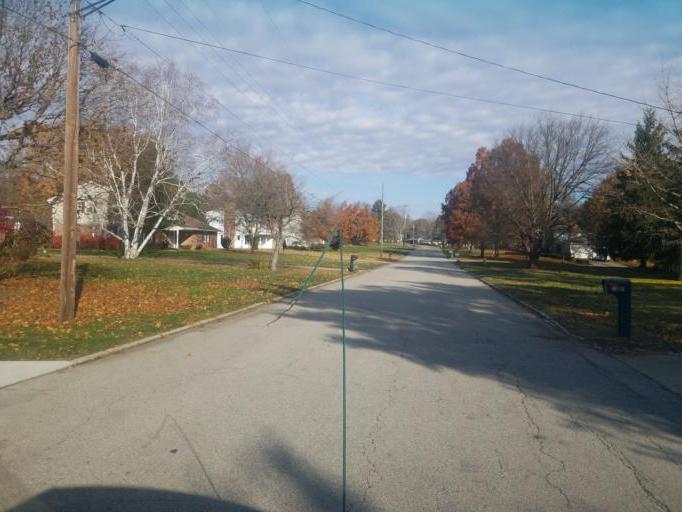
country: US
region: Ohio
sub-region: Richland County
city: Lexington
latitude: 40.7209
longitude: -82.5526
